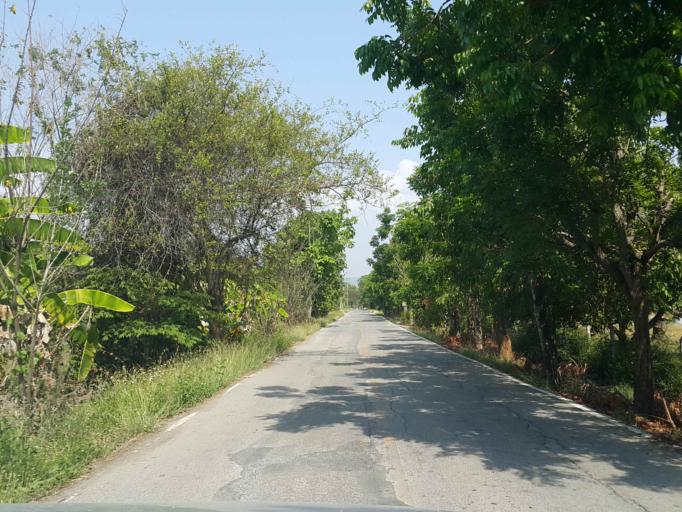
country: TH
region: Chiang Mai
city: San Kamphaeng
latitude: 18.7935
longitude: 99.1456
